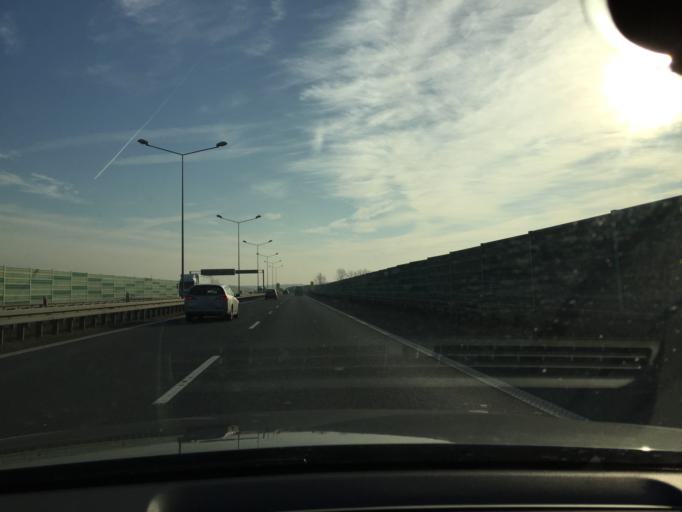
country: PL
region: Silesian Voivodeship
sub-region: Powiat gliwicki
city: Sosnicowice
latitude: 50.2775
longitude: 18.5732
